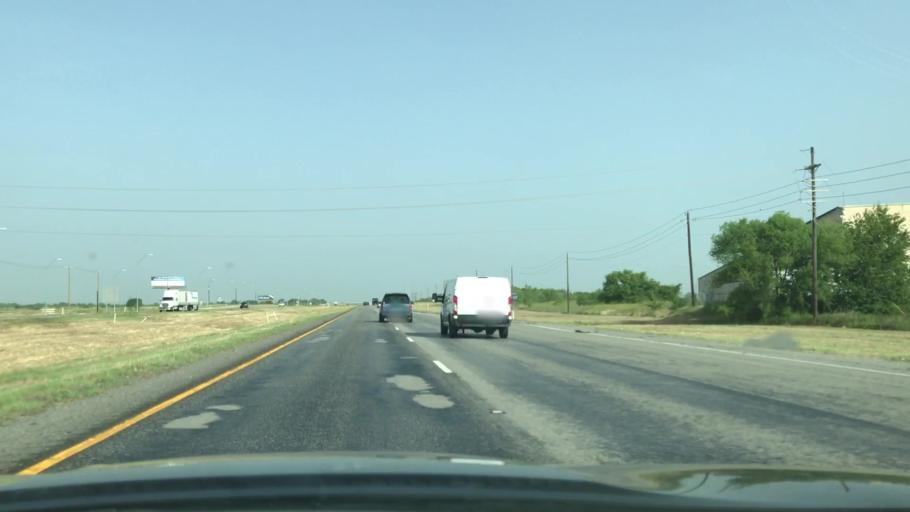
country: US
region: Texas
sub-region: Kaufman County
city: Terrell
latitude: 32.7229
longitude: -96.3241
